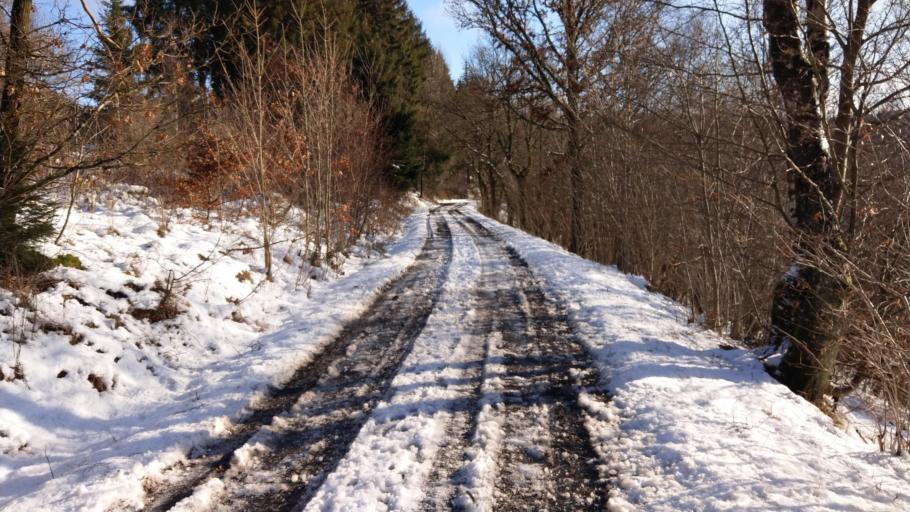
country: DE
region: North Rhine-Westphalia
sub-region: Regierungsbezirk Koln
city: Monschau
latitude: 50.5169
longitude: 6.2841
